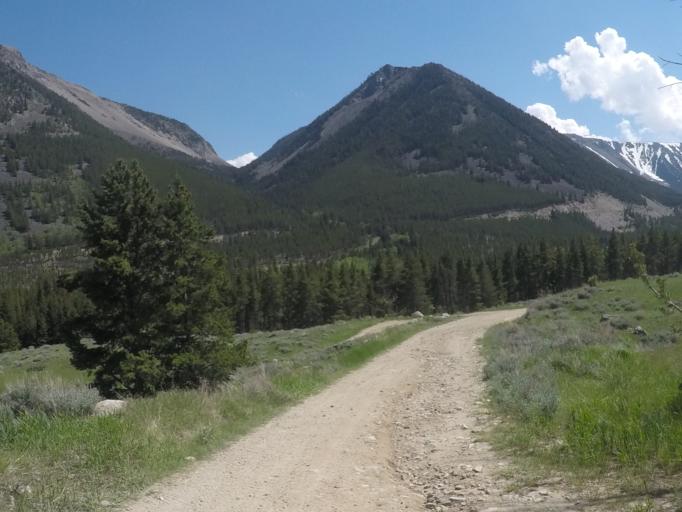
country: US
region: Montana
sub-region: Carbon County
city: Red Lodge
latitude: 45.0618
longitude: -109.4098
